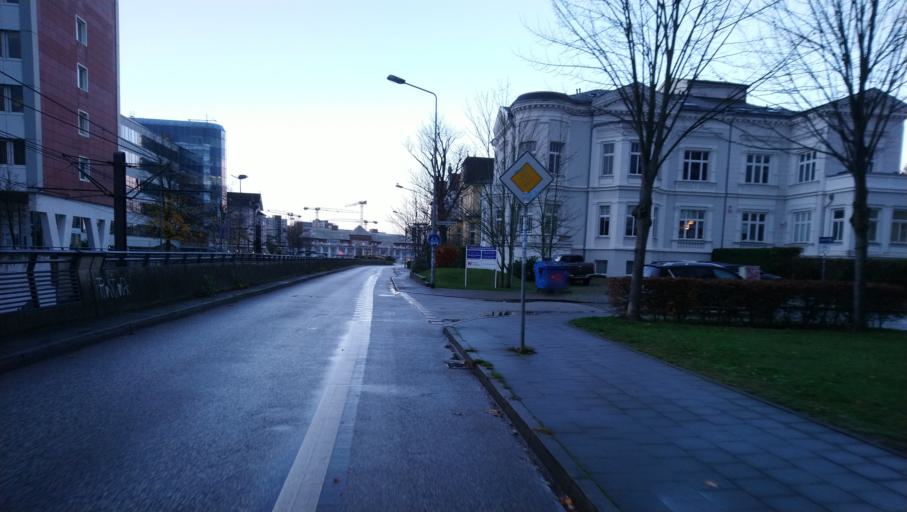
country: DE
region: Mecklenburg-Vorpommern
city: Rostock
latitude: 54.0787
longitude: 12.1378
